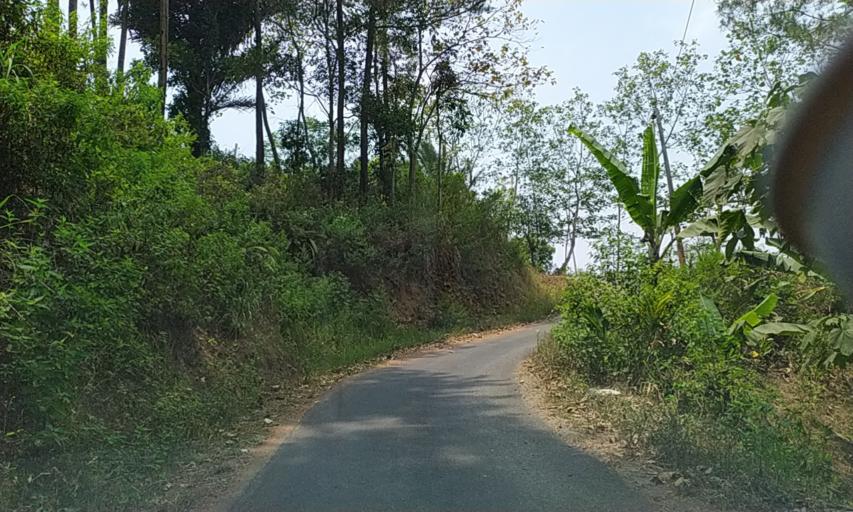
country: ID
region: Central Java
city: Jambuluwuk
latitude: -7.3290
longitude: 108.9309
